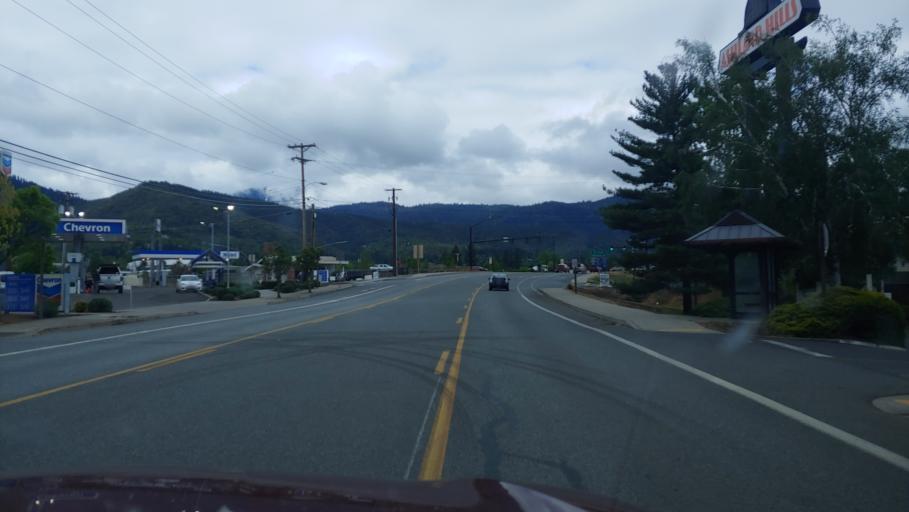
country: US
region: Oregon
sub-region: Jackson County
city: Ashland
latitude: 42.1858
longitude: -122.6632
